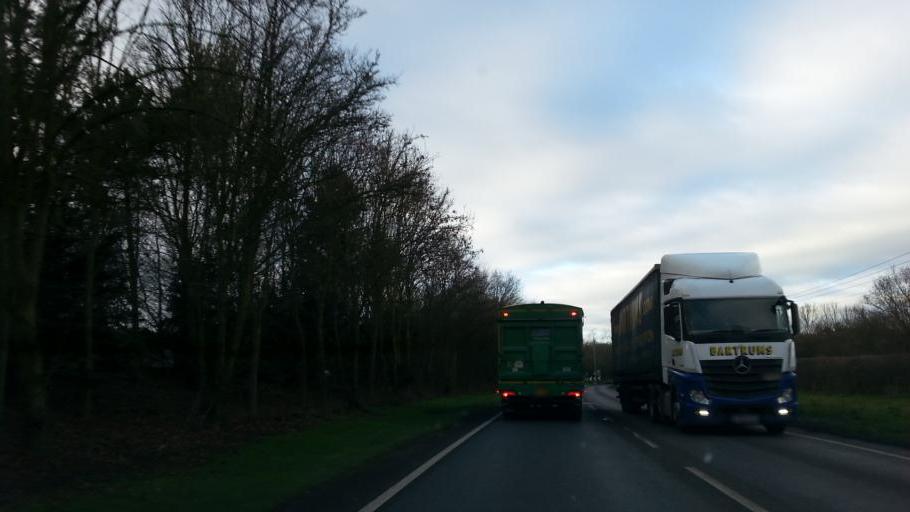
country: GB
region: England
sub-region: Suffolk
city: Bury St Edmunds
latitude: 52.2565
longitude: 0.7328
